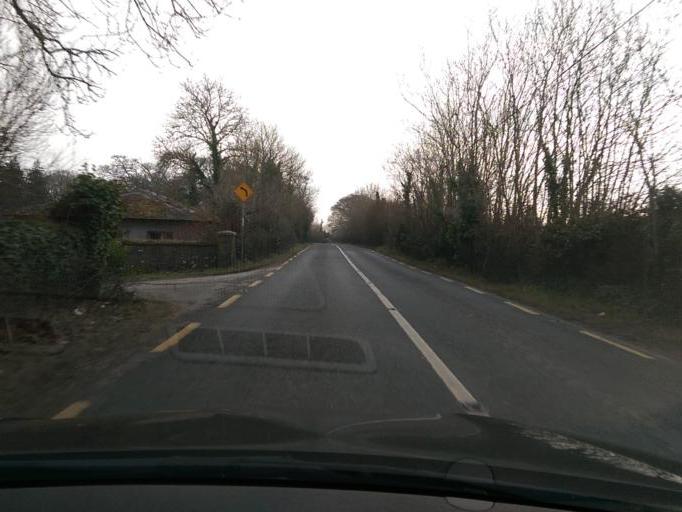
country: IE
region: Leinster
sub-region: An Iarmhi
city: Athlone
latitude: 53.4607
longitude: -7.8760
